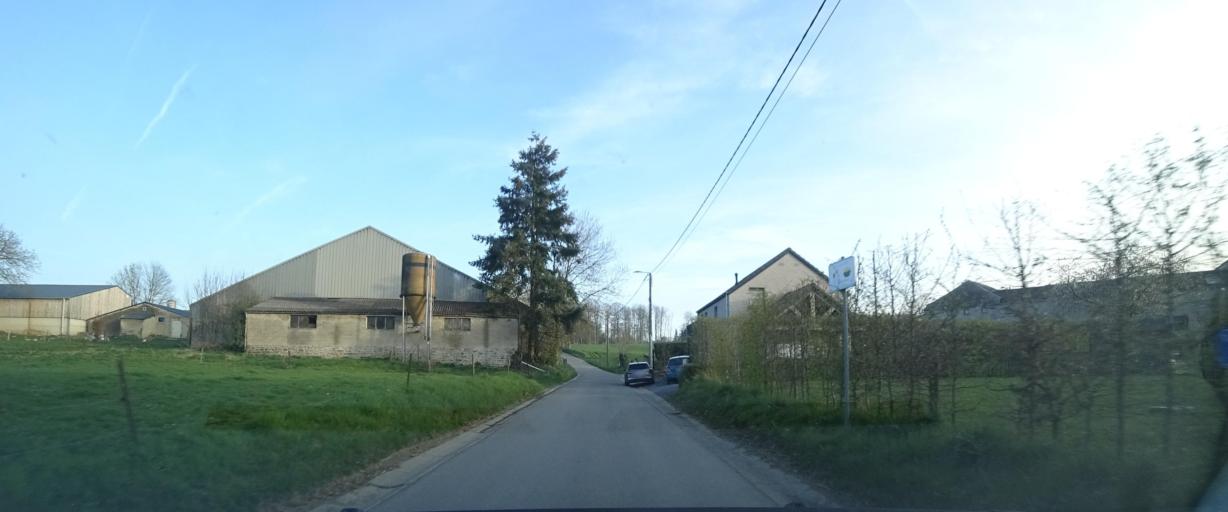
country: BE
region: Wallonia
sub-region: Province de Namur
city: Hamois
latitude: 50.3165
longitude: 5.1527
